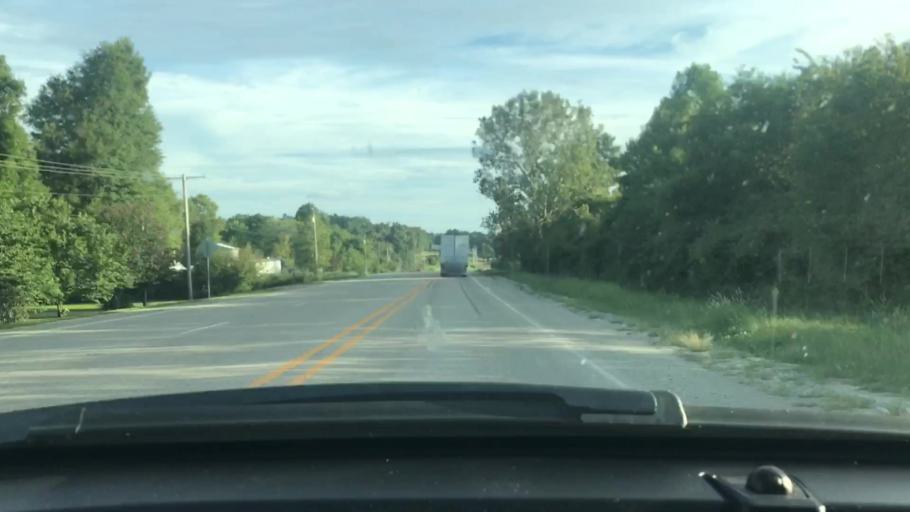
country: US
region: Arkansas
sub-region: Lawrence County
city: Hoxie
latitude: 36.1412
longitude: -91.1581
